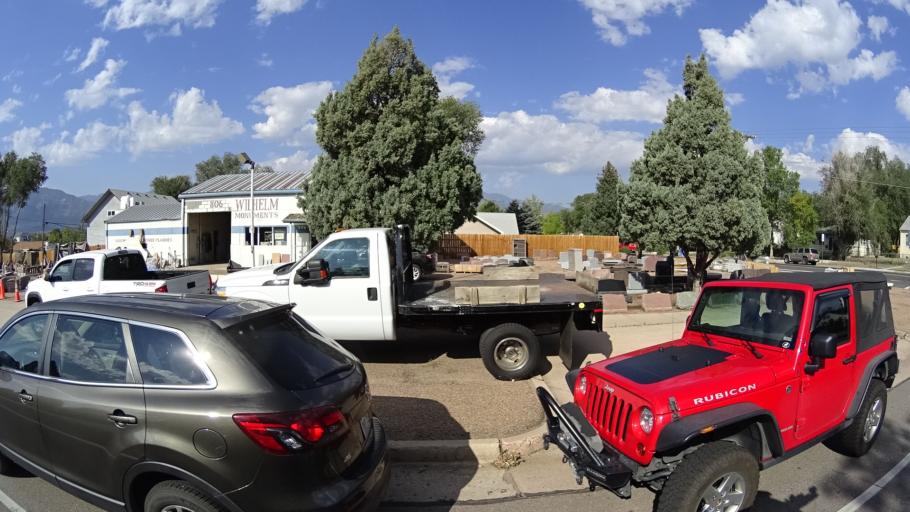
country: US
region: Colorado
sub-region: El Paso County
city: Colorado Springs
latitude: 38.8221
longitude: -104.8044
